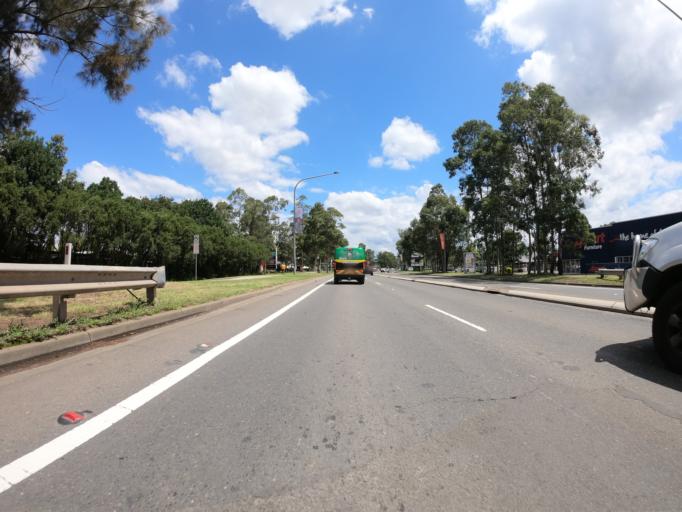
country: AU
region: New South Wales
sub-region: Penrith Municipality
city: Glenmore Park
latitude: -33.7680
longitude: 150.6779
